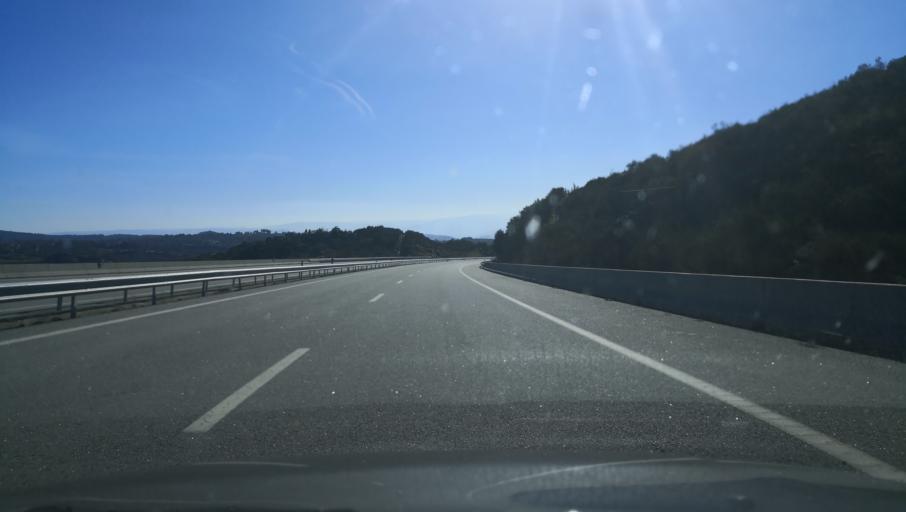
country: PT
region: Vila Real
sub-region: Vila Real
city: Vila Real
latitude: 41.3774
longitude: -7.6683
